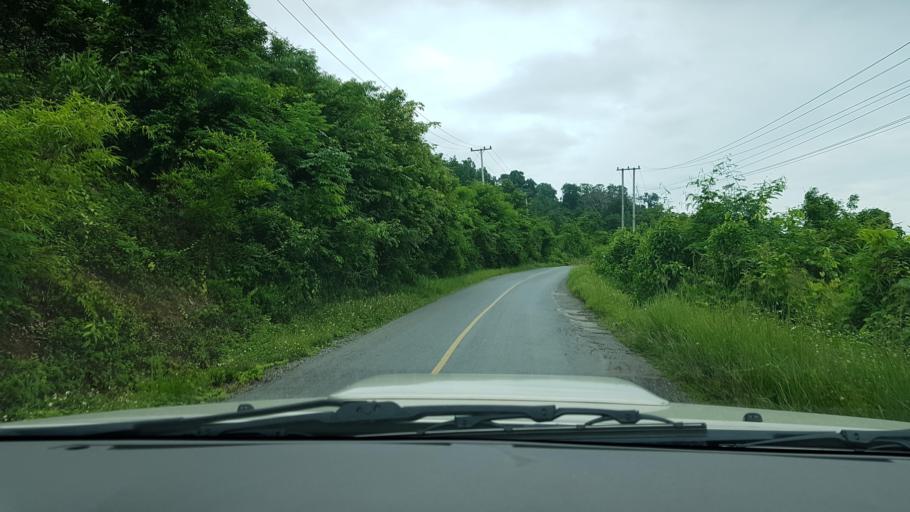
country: LA
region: Loungnamtha
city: Muang Nale
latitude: 20.1794
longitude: 101.5189
